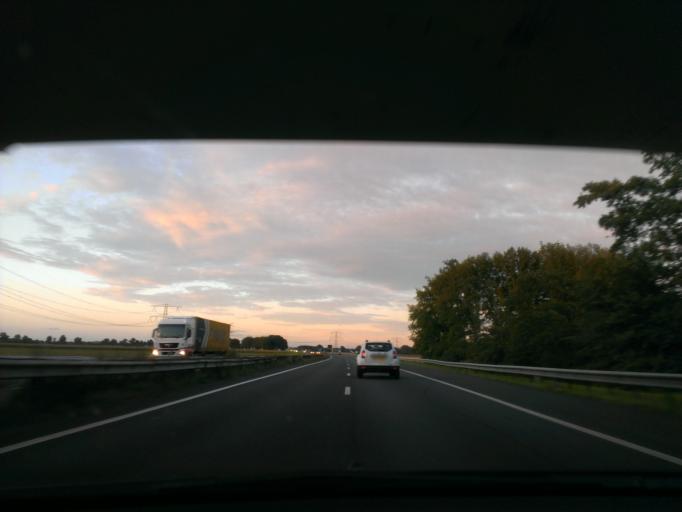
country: NL
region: South Holland
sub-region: Gemeente Binnenmaas
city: Mijnsheerenland
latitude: 51.8038
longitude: 4.4663
